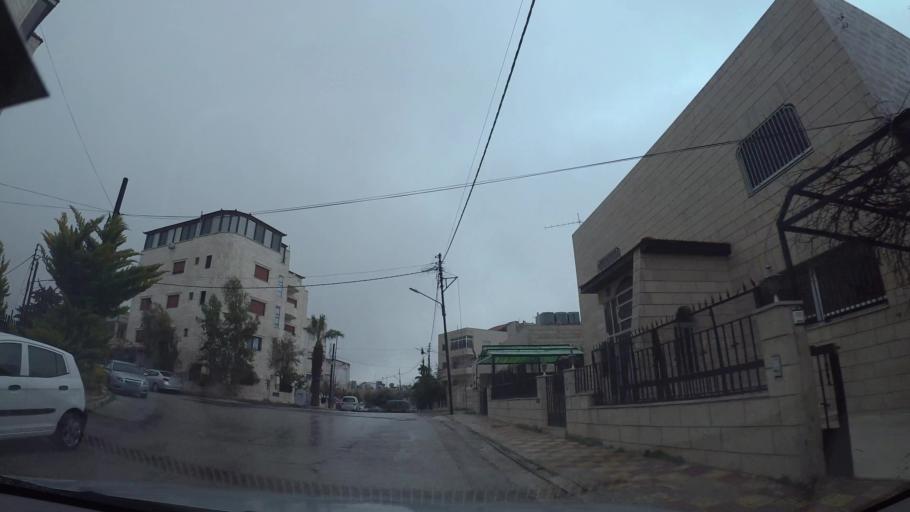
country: JO
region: Amman
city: Al Jubayhah
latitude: 32.0291
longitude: 35.8507
